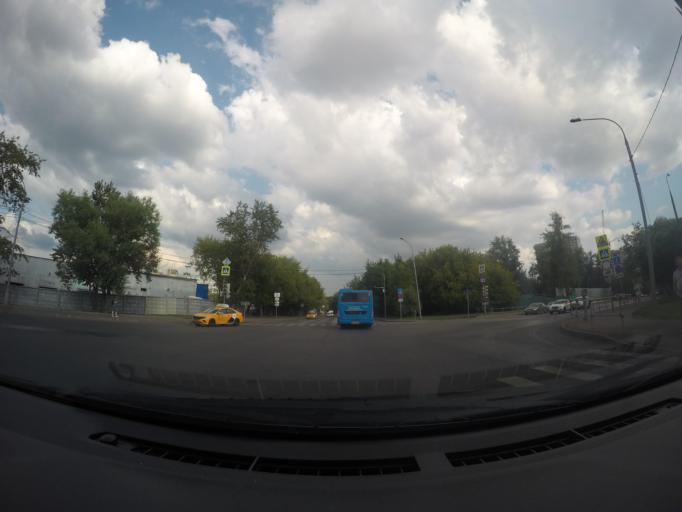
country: RU
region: Moscow
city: Kozeyevo
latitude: 55.8593
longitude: 37.6201
